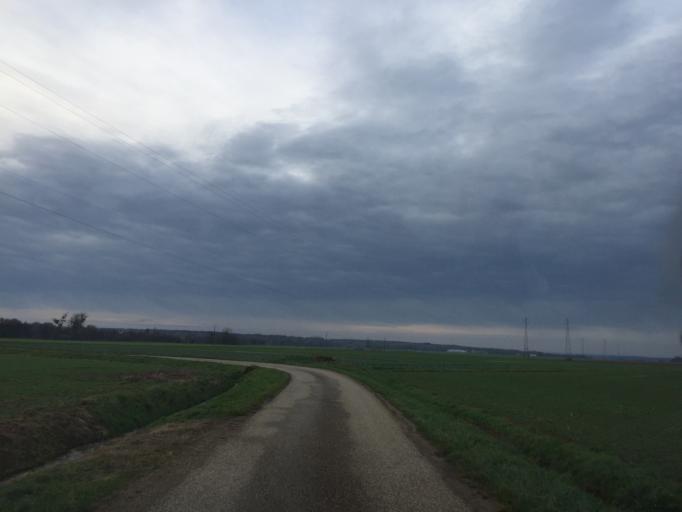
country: FR
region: Franche-Comte
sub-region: Departement du Jura
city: Mont-sous-Vaudrey
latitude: 46.9389
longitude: 5.6788
